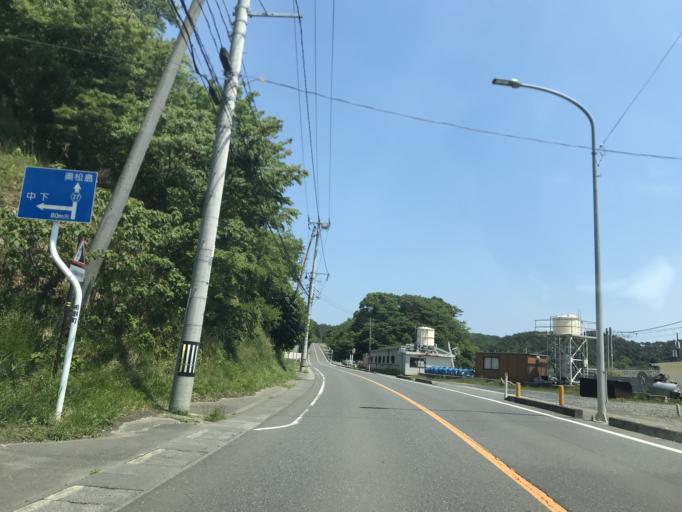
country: JP
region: Miyagi
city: Matsushima
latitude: 38.3788
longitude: 141.1305
